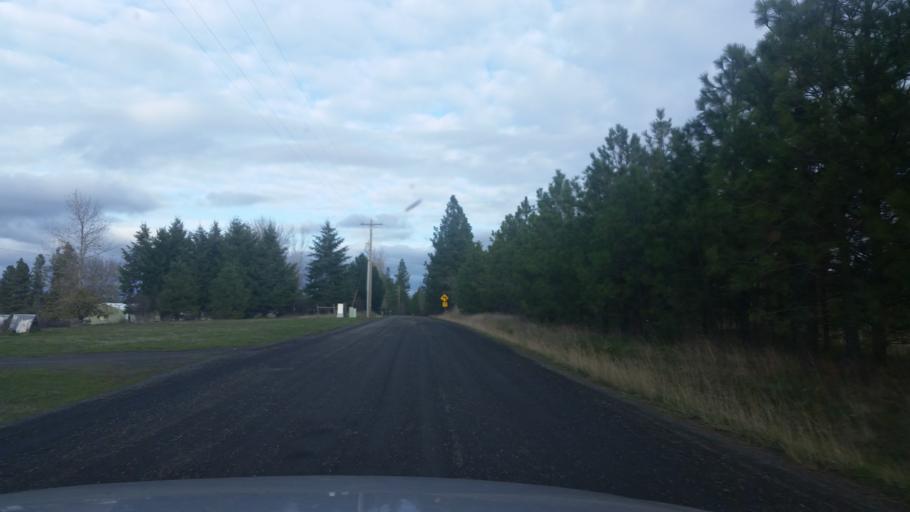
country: US
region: Washington
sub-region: Spokane County
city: Cheney
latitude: 47.4245
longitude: -117.4666
